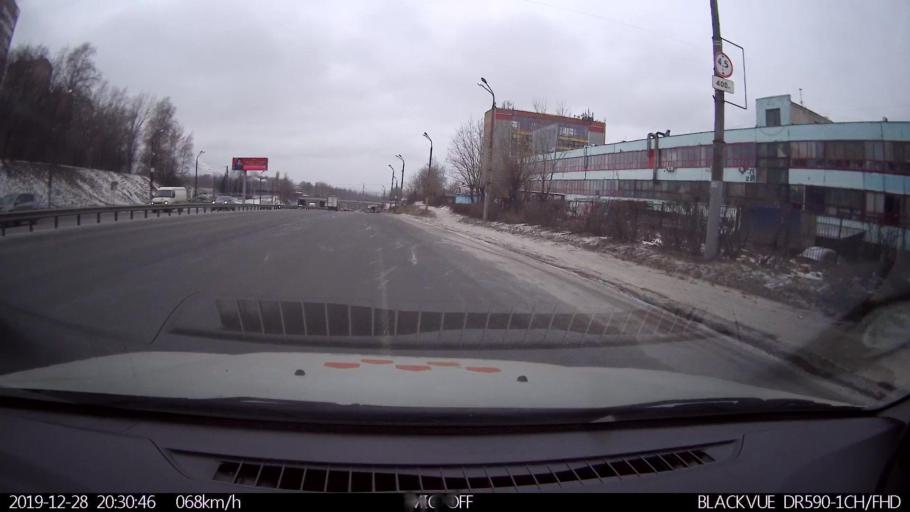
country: RU
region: Nizjnij Novgorod
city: Nizhniy Novgorod
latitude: 56.2417
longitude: 43.9696
